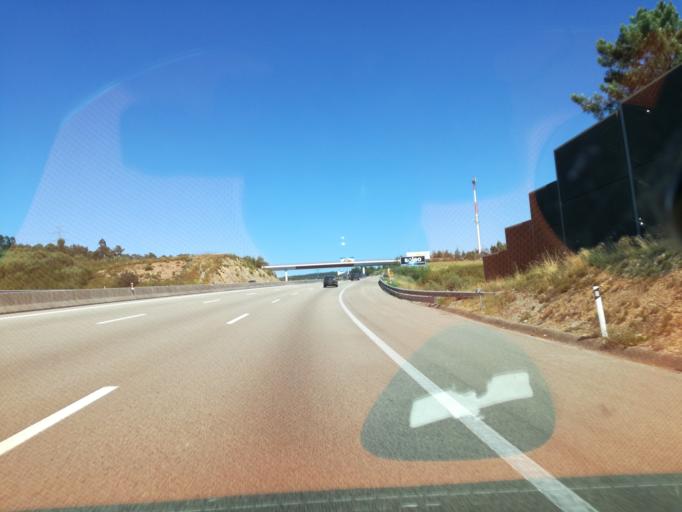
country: PT
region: Porto
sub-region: Trofa
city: Sao Romao do Coronado
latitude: 41.3052
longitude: -8.5368
